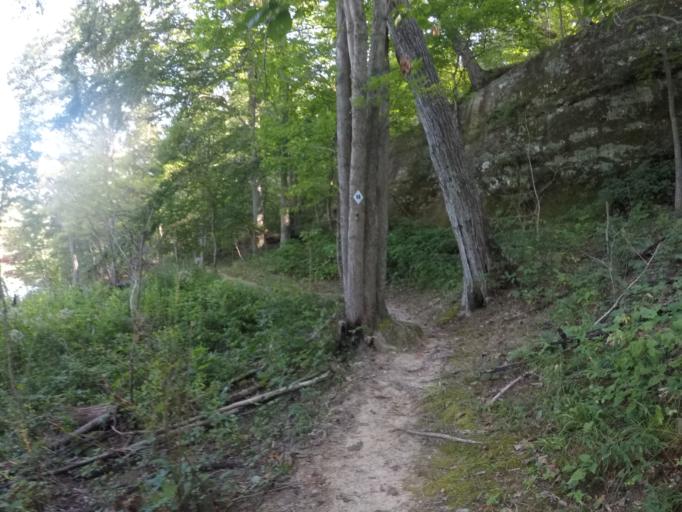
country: US
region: Ohio
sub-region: Lawrence County
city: Ironton
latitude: 38.6125
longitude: -82.6272
